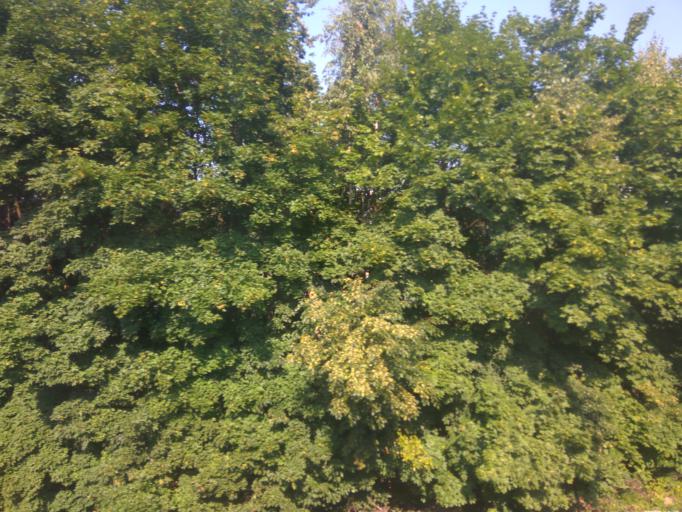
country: RU
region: Moscow
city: Annino
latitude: 55.5697
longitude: 37.6098
